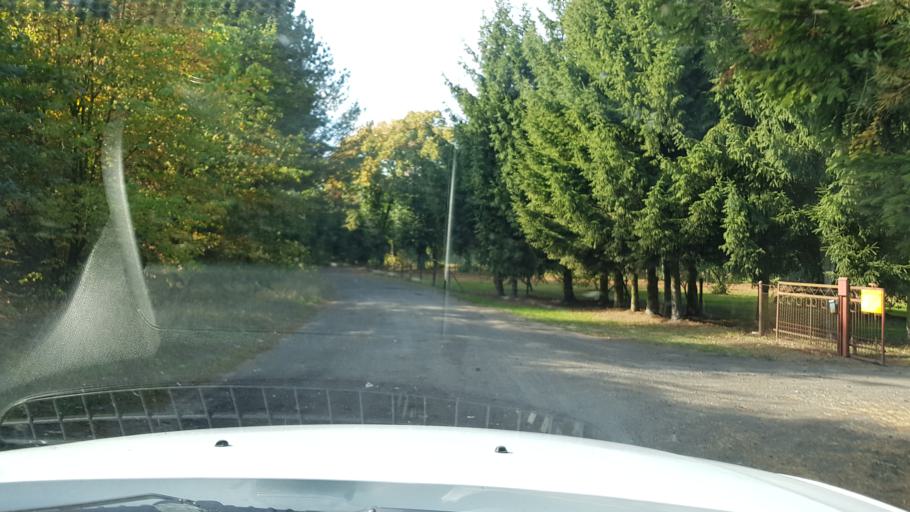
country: PL
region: West Pomeranian Voivodeship
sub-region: Powiat pyrzycki
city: Lipiany
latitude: 52.9333
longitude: 14.9510
